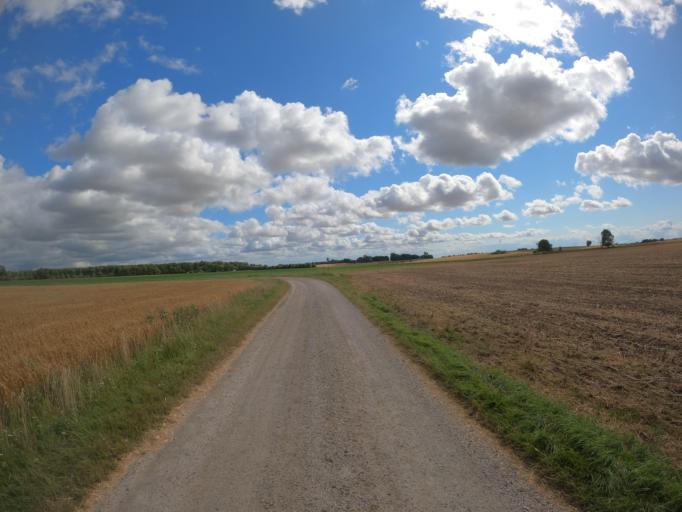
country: SE
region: Skane
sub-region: Lunds Kommun
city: Lund
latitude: 55.7277
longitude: 13.2626
